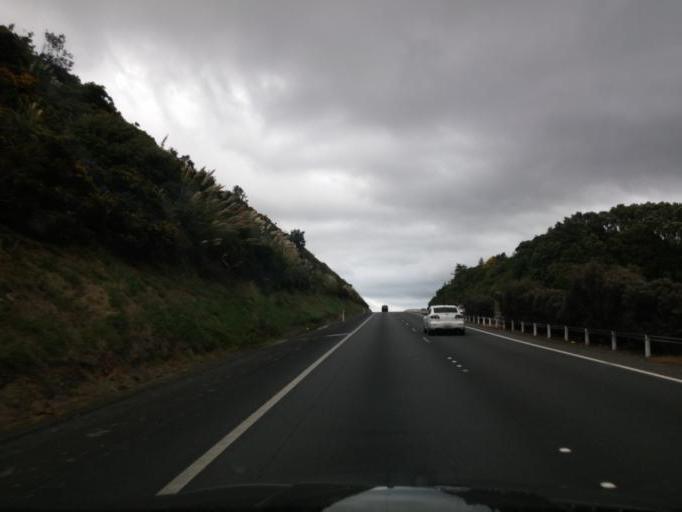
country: NZ
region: Wellington
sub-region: Porirua City
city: Porirua
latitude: -41.1695
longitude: 174.8318
